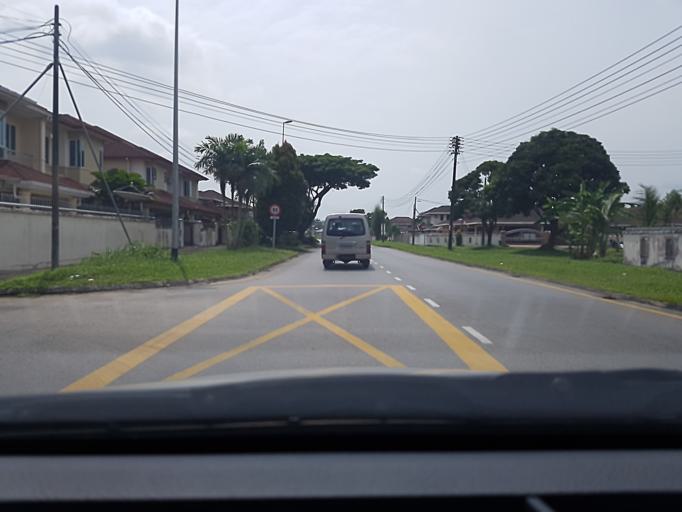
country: MY
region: Sarawak
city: Kuching
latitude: 1.5222
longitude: 110.3704
